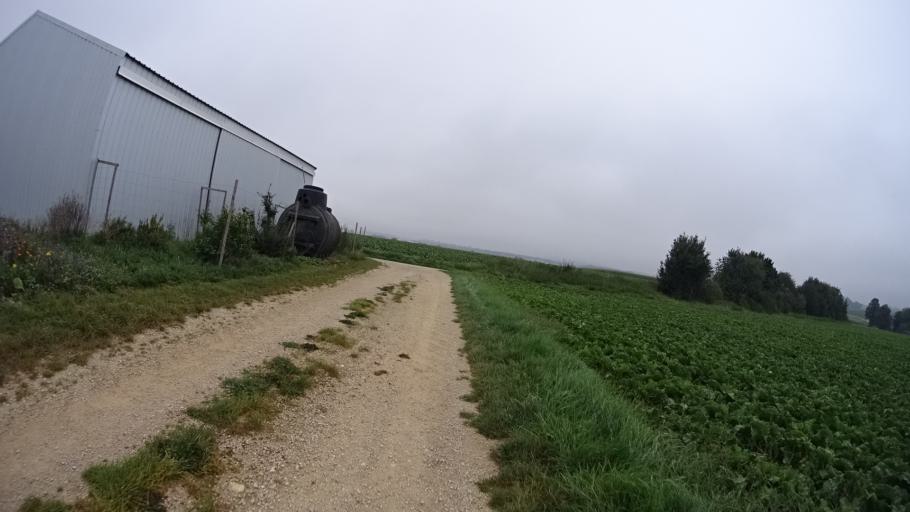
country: DE
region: Bavaria
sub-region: Upper Bavaria
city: Hepberg
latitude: 48.8261
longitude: 11.4819
